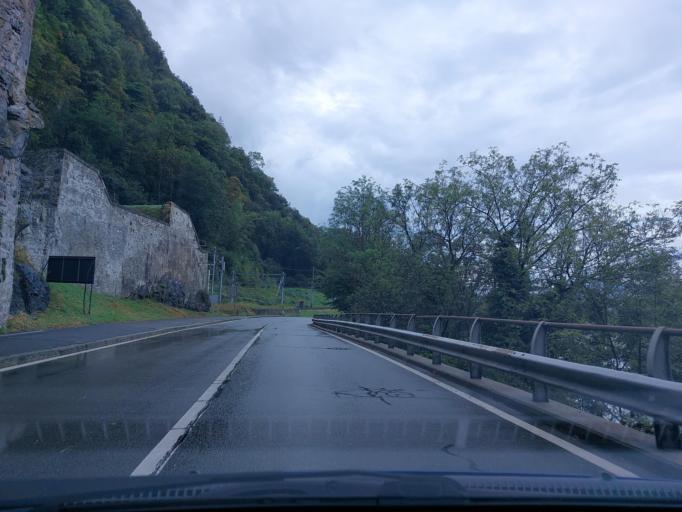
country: CH
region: Valais
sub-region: Saint-Maurice District
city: Saint-Maurice
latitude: 46.2235
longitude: 7.0030
